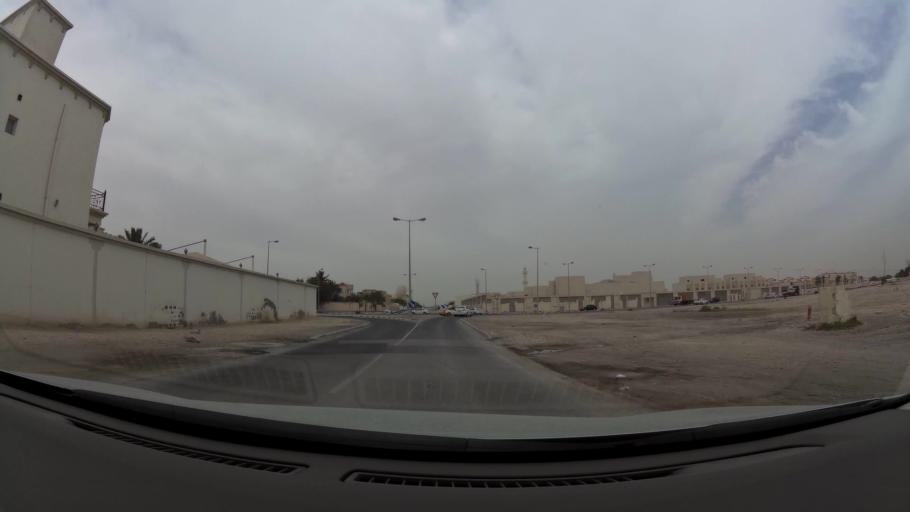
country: QA
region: Baladiyat ar Rayyan
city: Ar Rayyan
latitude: 25.2258
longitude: 51.4595
